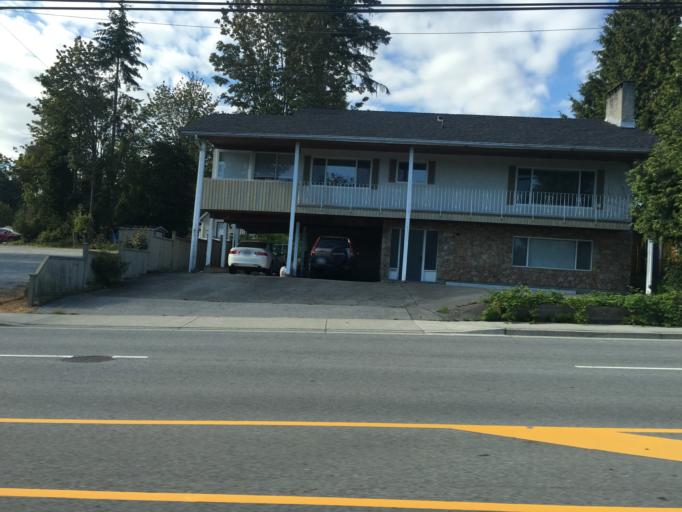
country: CA
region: British Columbia
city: Port Moody
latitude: 49.2490
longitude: -122.8542
